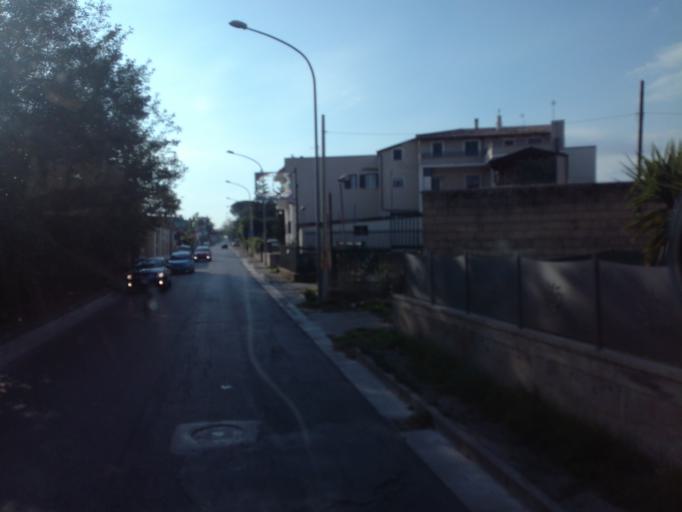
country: IT
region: Campania
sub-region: Provincia di Napoli
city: Giugliano in Campania
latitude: 40.9427
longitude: 14.1813
